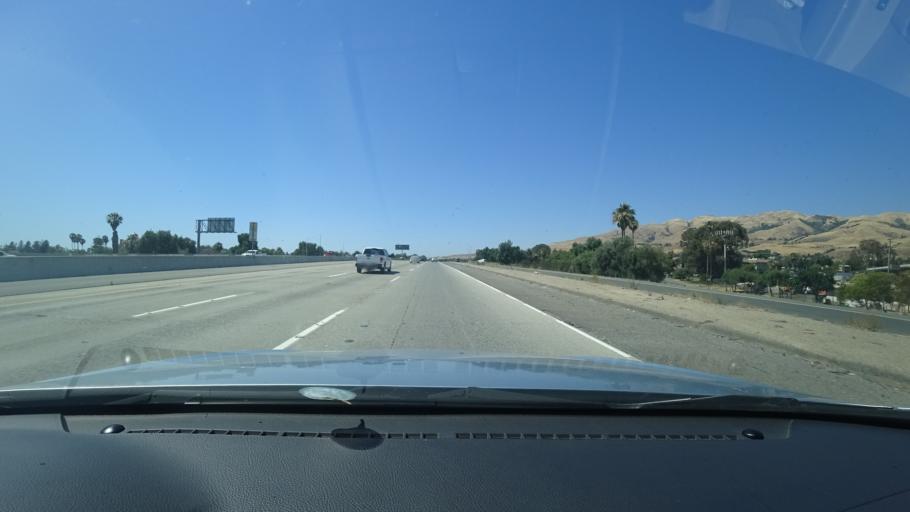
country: US
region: California
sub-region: Santa Clara County
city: Milpitas
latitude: 37.4327
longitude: -121.8872
